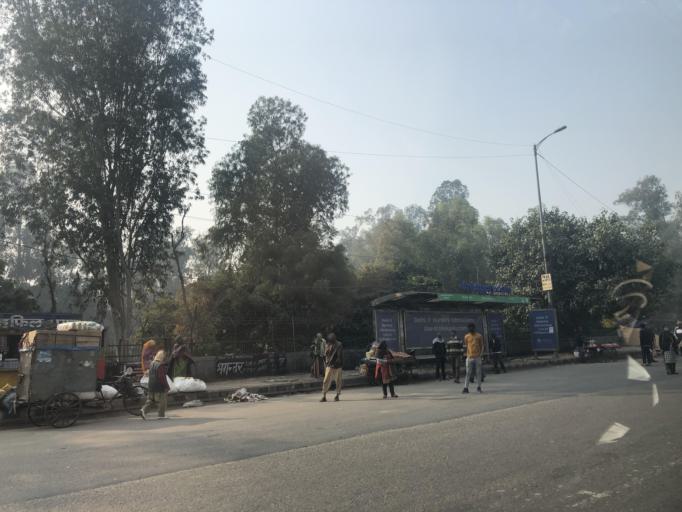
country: IN
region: NCT
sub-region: West Delhi
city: Nangloi Jat
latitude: 28.6792
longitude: 77.0964
